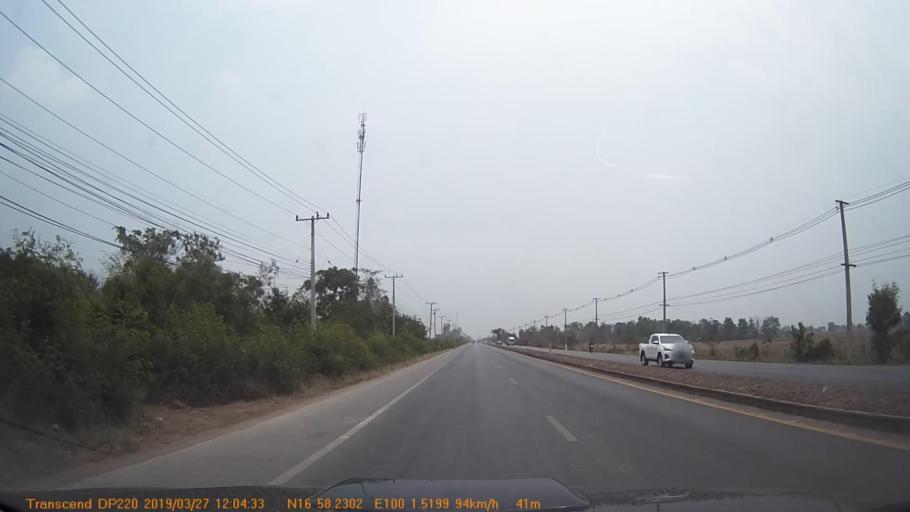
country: TH
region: Sukhothai
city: Kong Krailat
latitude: 16.9704
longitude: 100.0258
